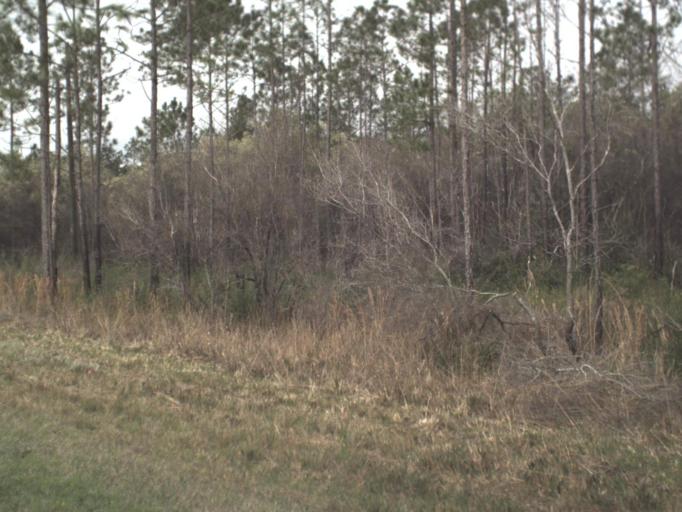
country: US
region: Florida
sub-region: Gulf County
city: Wewahitchka
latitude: 30.1356
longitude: -84.9851
